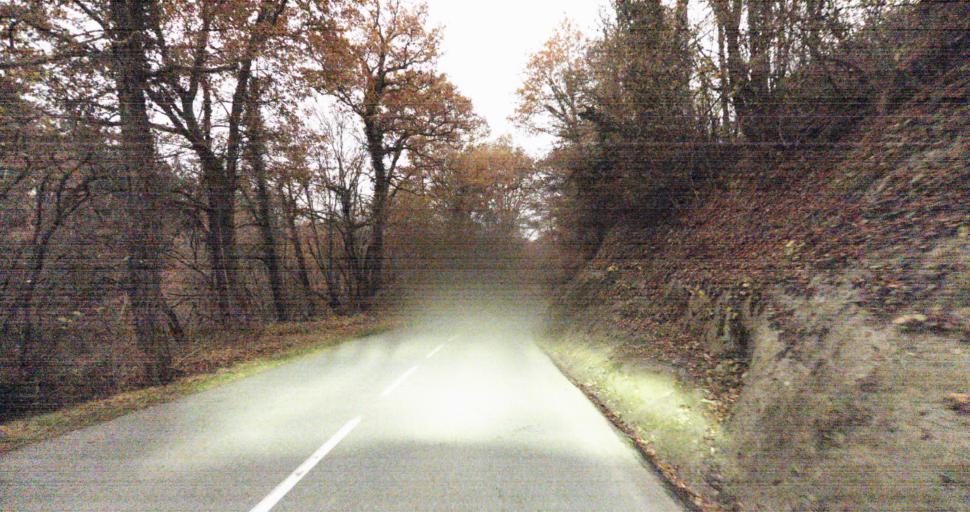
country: FR
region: Rhone-Alpes
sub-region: Departement de la Haute-Savoie
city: Alby-sur-Cheran
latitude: 45.8298
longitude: 6.0238
